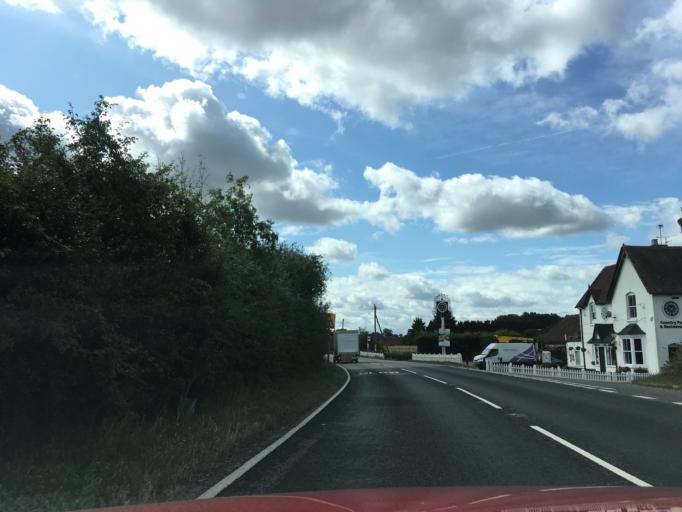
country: GB
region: England
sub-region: Kent
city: Marden
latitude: 51.2021
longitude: 0.5169
